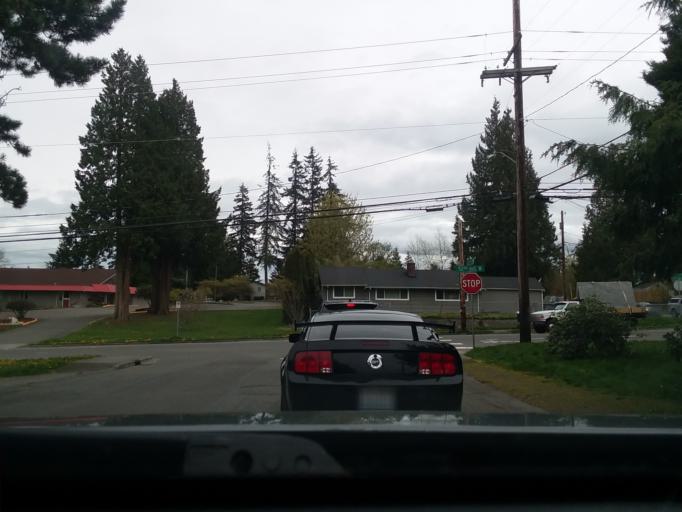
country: US
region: Washington
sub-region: Snohomish County
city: Mountlake Terrace
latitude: 47.8029
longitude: -122.3036
